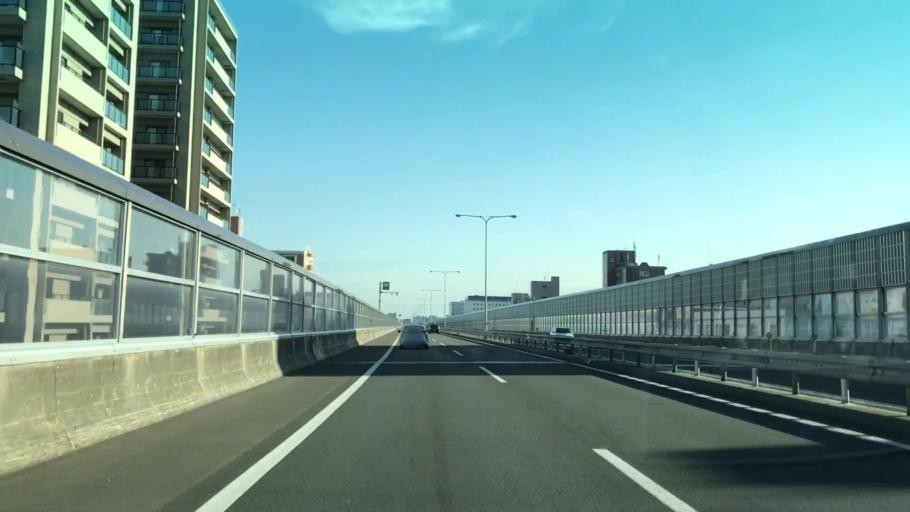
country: JP
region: Hokkaido
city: Sapporo
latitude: 43.1003
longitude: 141.3375
